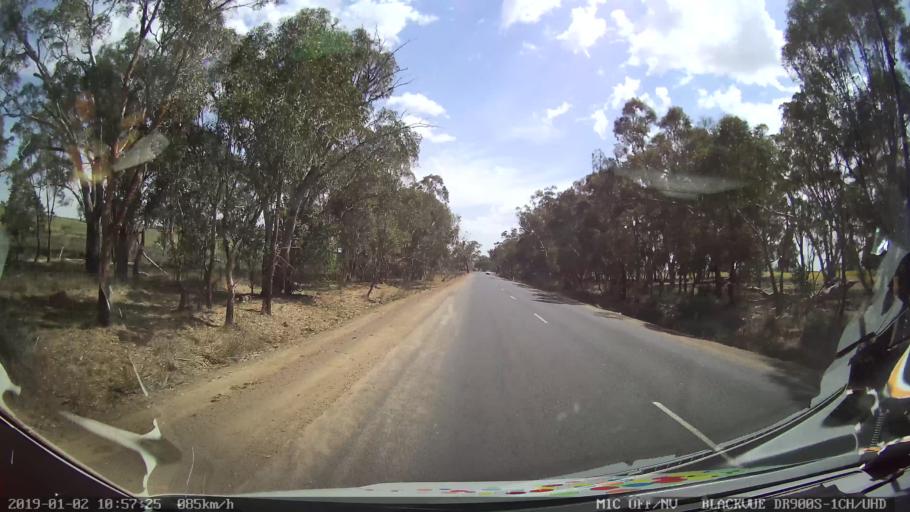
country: AU
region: New South Wales
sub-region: Cootamundra
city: Cootamundra
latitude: -34.6356
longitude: 148.2825
